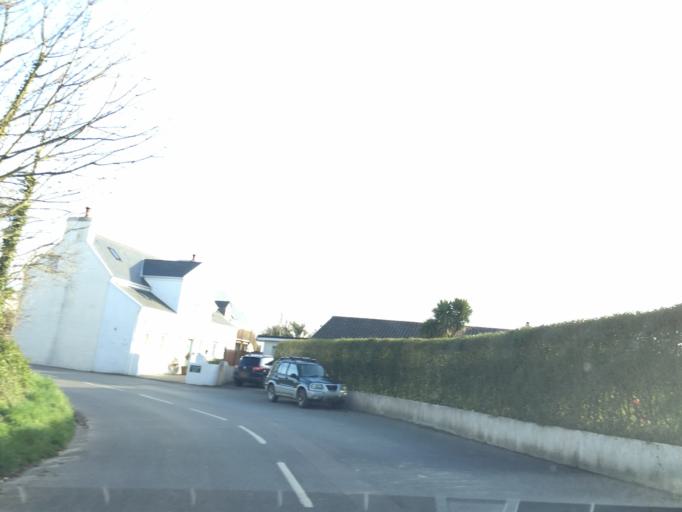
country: JE
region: St Helier
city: Saint Helier
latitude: 49.2450
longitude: -2.0985
